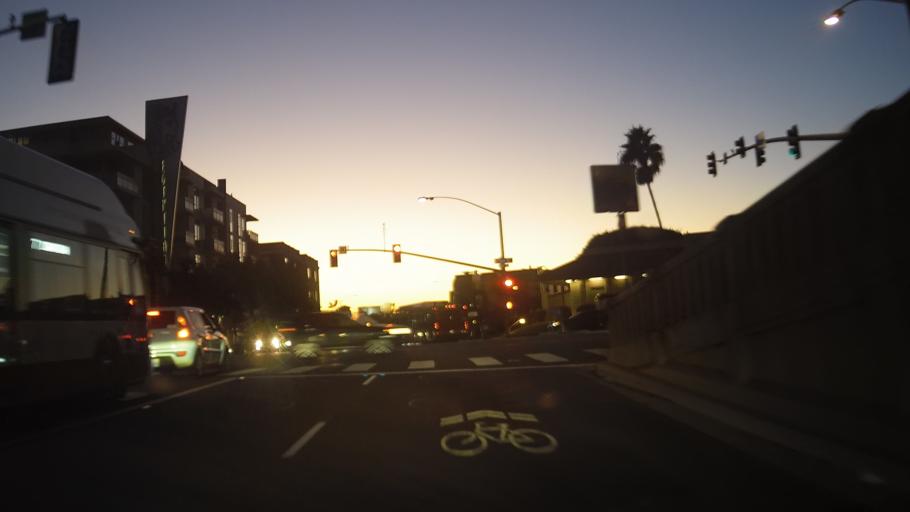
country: US
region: California
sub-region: San Diego County
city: San Diego
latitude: 32.7485
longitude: -117.1459
